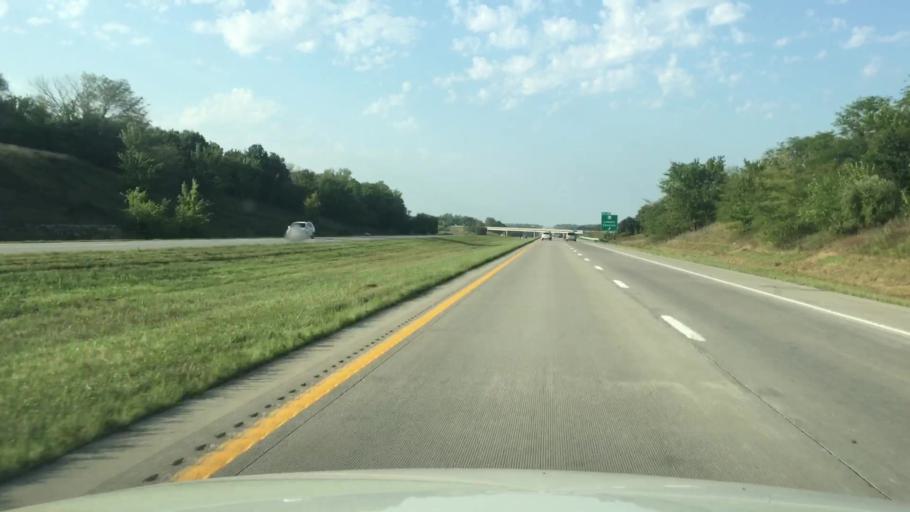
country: US
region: Missouri
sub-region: Clinton County
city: Cameron
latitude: 39.6621
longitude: -94.2370
